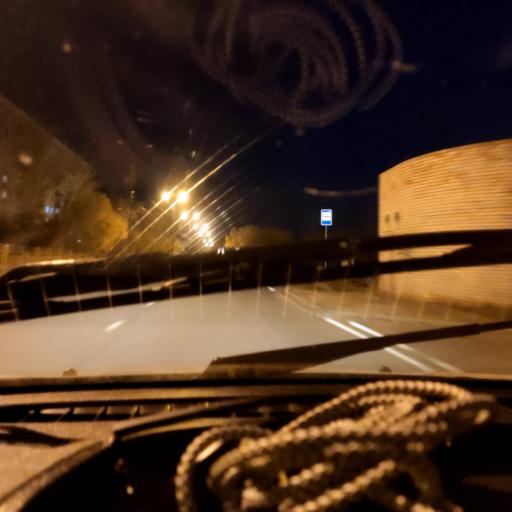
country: RU
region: Samara
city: Zhigulevsk
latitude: 53.4681
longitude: 49.5369
